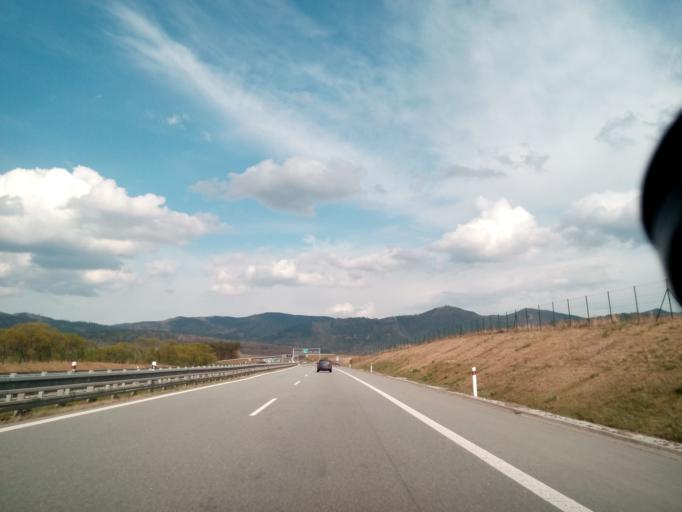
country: SK
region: Presovsky
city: Spisske Podhradie
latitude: 49.0066
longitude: 20.7883
